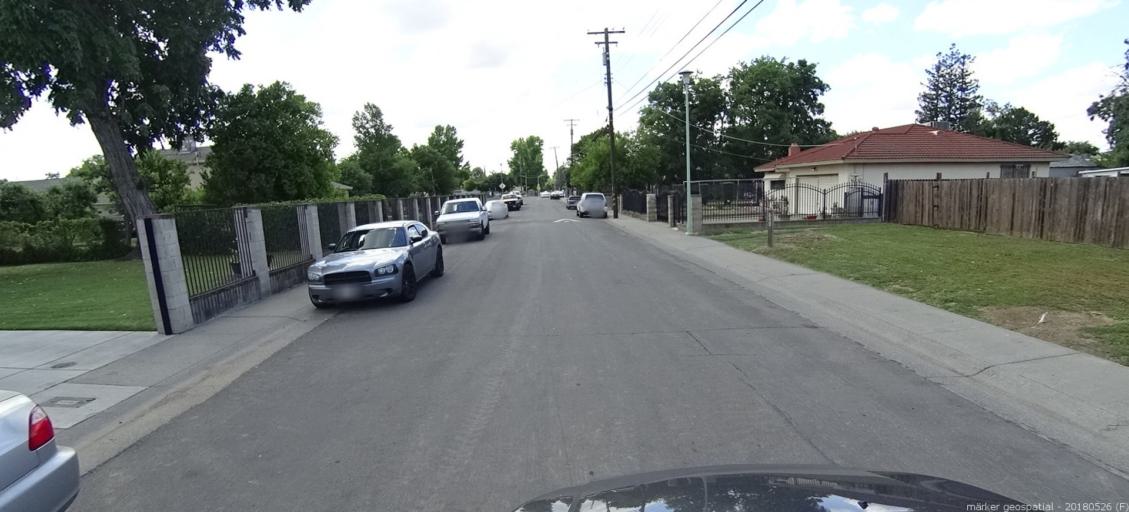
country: US
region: California
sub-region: Sacramento County
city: Sacramento
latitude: 38.6158
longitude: -121.4738
